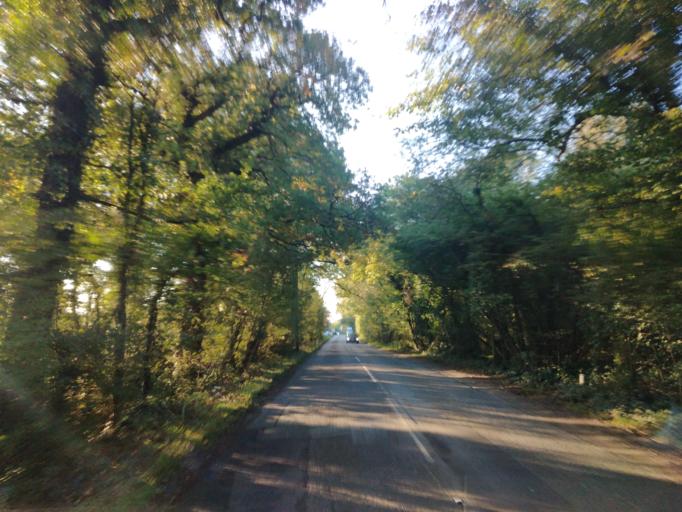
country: GB
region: England
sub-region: West Sussex
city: Goring-by-Sea
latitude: 50.8311
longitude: -0.4357
